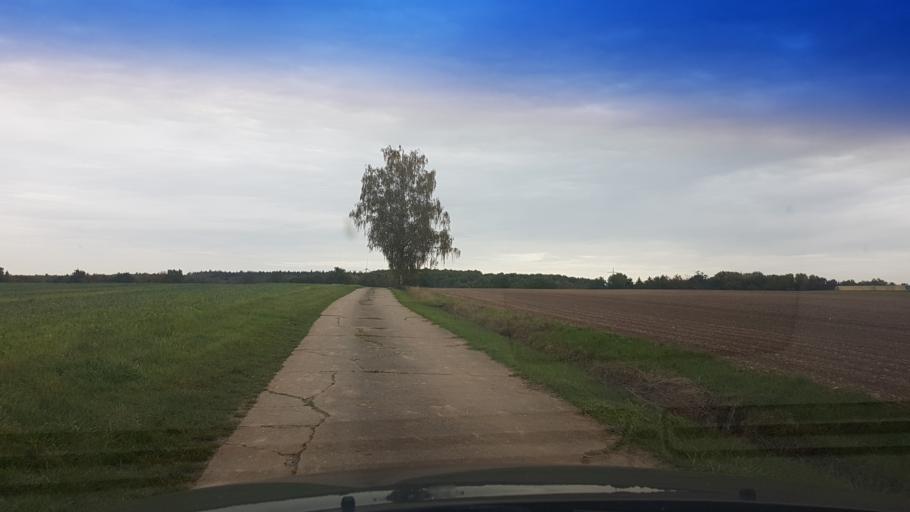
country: DE
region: Bavaria
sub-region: Upper Franconia
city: Zapfendorf
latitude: 49.9786
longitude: 10.9343
